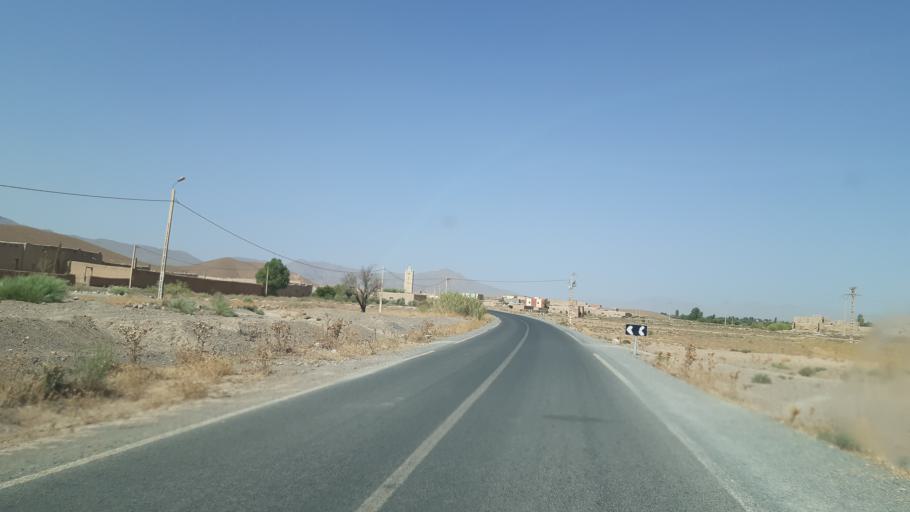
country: MA
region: Meknes-Tafilalet
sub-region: Errachidia
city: Errachidia
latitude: 32.2515
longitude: -4.5775
